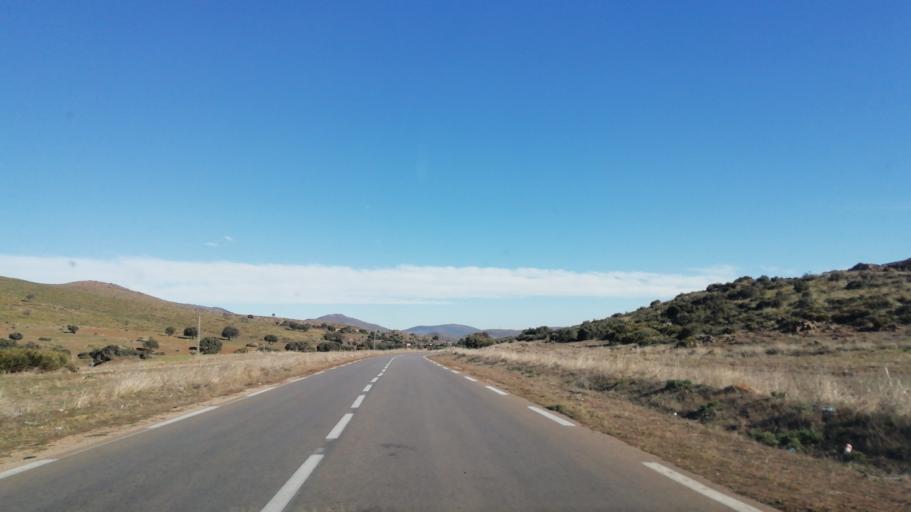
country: DZ
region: Tlemcen
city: Ouled Mimoun
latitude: 34.7520
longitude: -1.1557
